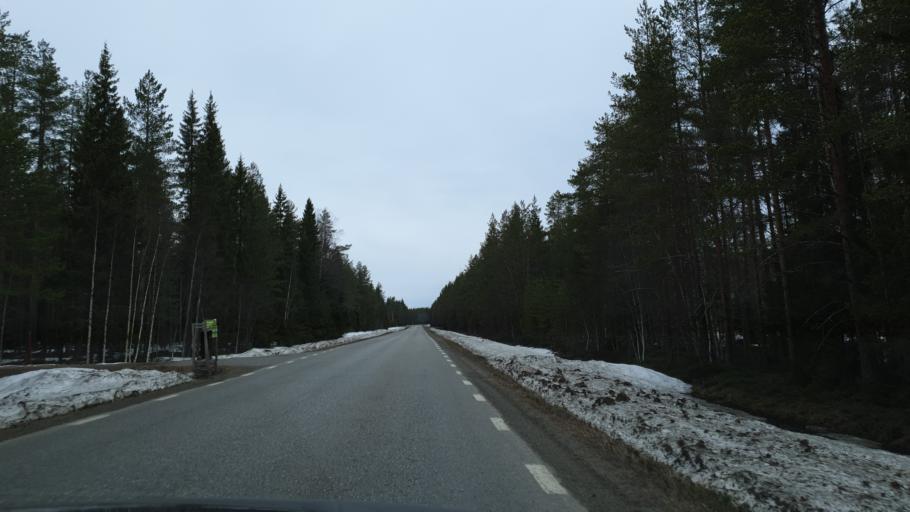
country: SE
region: Vaesterbotten
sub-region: Robertsfors Kommun
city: Robertsfors
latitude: 64.3969
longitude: 20.8881
